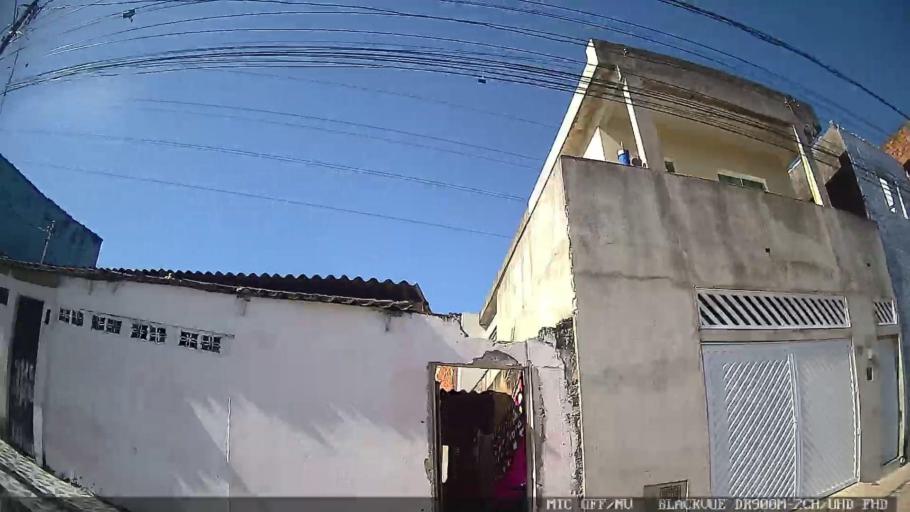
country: BR
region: Sao Paulo
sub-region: Guaruja
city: Guaruja
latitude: -23.9509
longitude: -46.2818
